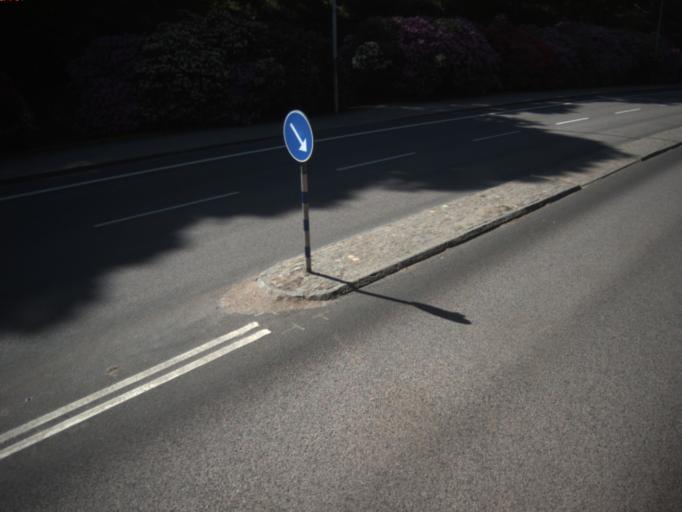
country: SE
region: Skane
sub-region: Helsingborg
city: Helsingborg
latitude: 56.0528
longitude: 12.6940
